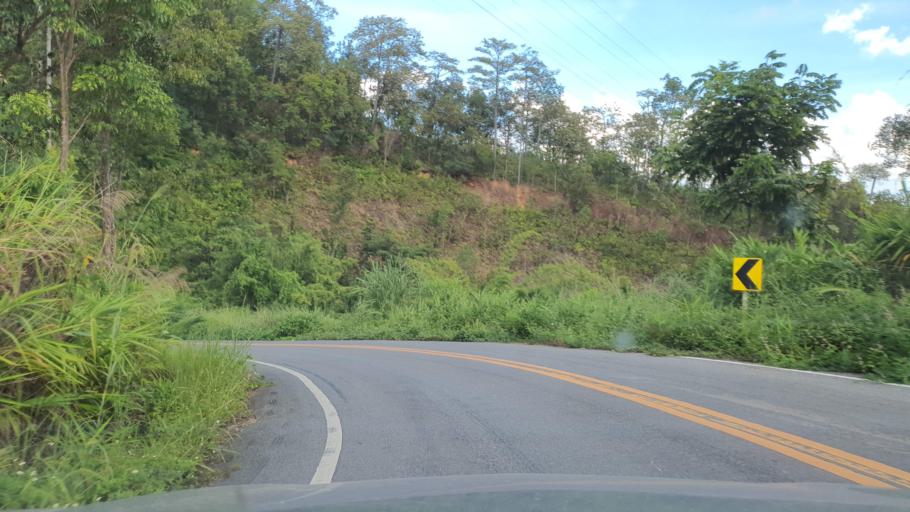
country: TH
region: Chiang Rai
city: Wiang Pa Pao
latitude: 19.3153
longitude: 99.3979
